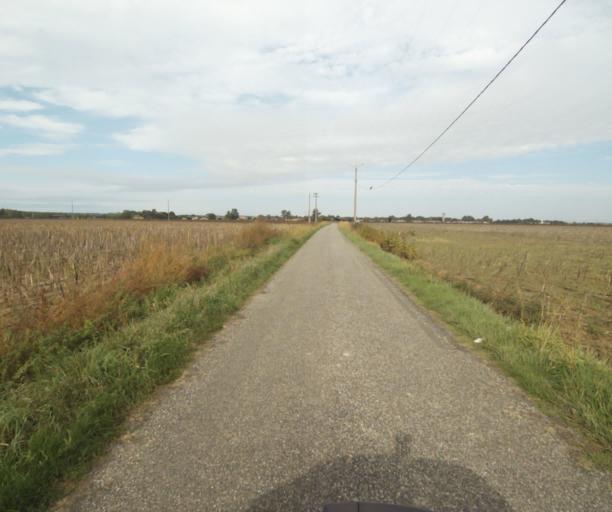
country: FR
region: Midi-Pyrenees
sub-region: Departement du Tarn-et-Garonne
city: Finhan
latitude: 43.9042
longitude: 1.2358
